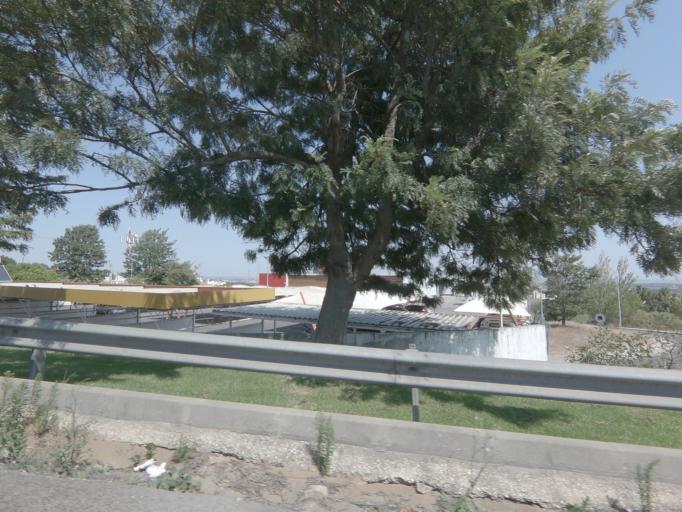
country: PT
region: Setubal
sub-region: Palmela
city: Palmela
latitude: 38.5750
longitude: -8.8889
